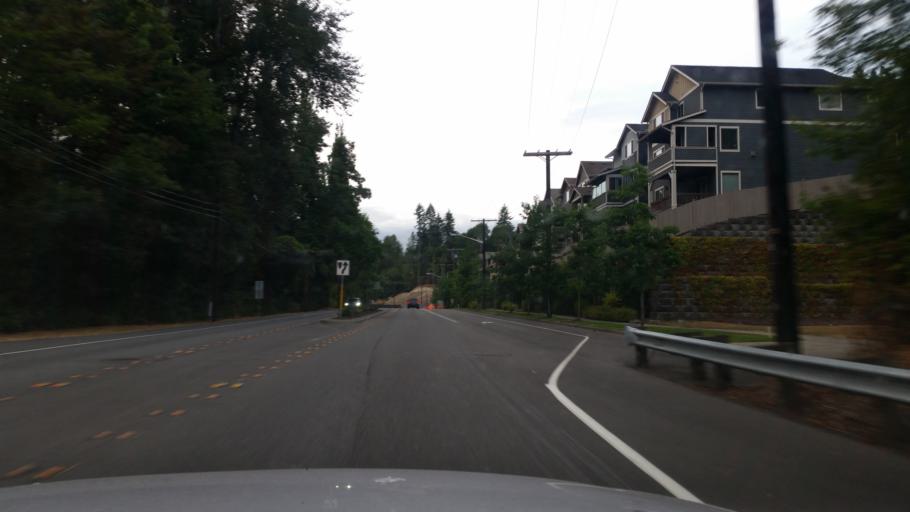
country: US
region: Washington
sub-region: King County
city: Bothell
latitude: 47.7729
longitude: -122.2159
